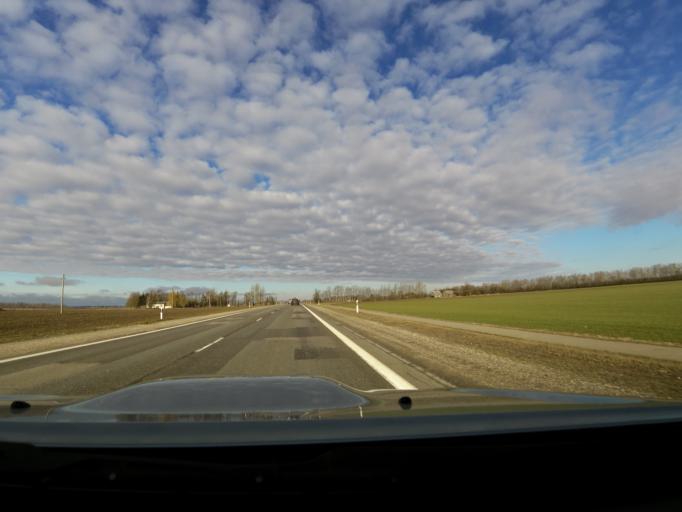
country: LT
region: Panevezys
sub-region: Panevezys City
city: Panevezys
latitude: 55.7362
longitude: 24.2083
